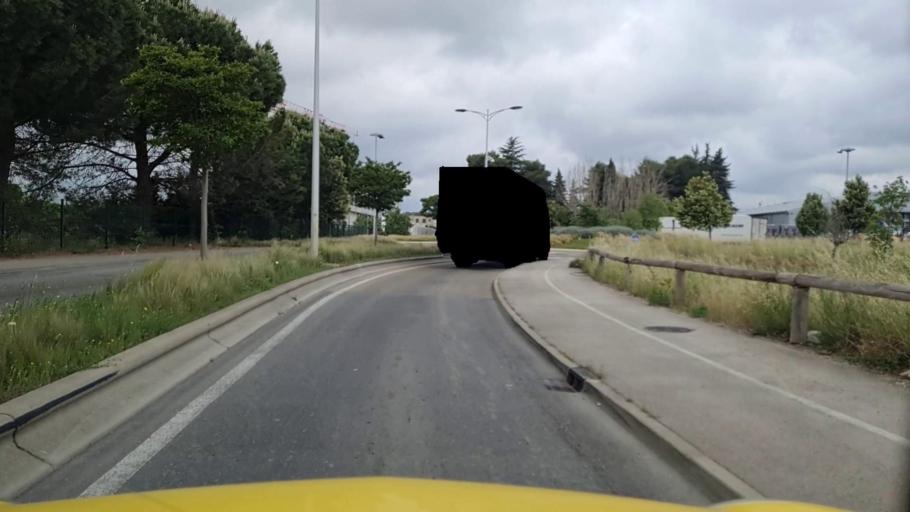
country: FR
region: Languedoc-Roussillon
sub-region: Departement du Gard
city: Milhaud
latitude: 43.8090
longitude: 4.3325
